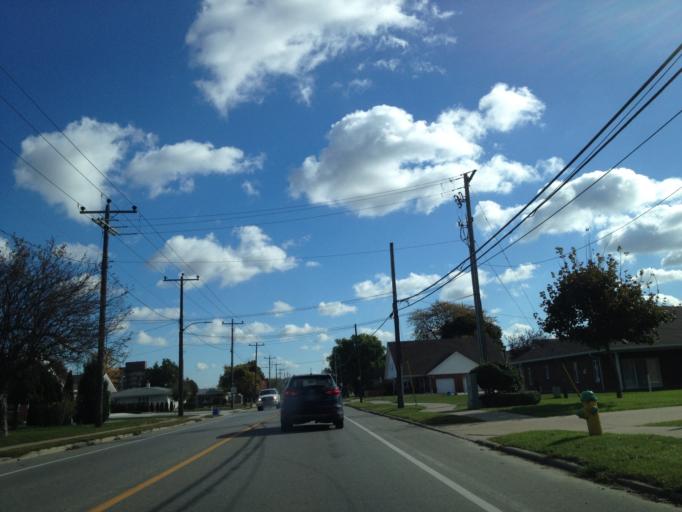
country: CA
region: Ontario
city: Amherstburg
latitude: 42.0462
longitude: -82.5908
